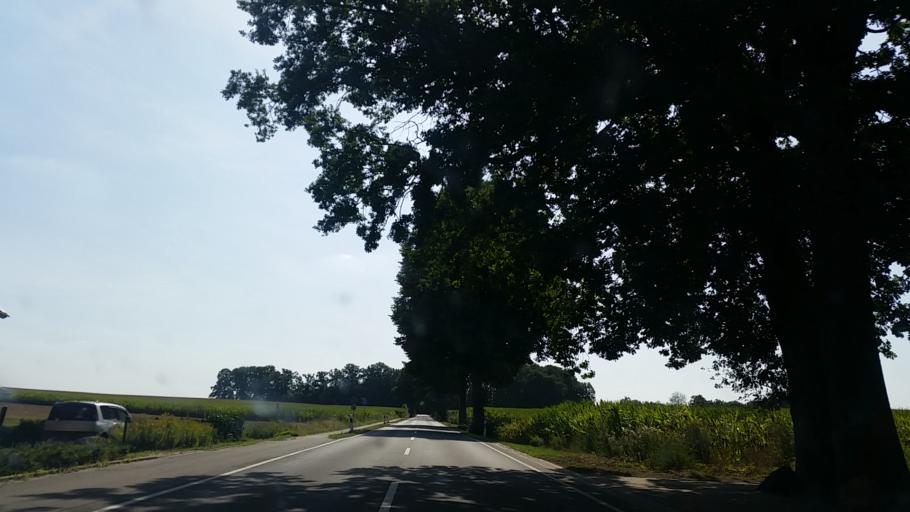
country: DE
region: Lower Saxony
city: Alfhausen
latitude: 52.5099
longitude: 7.9261
